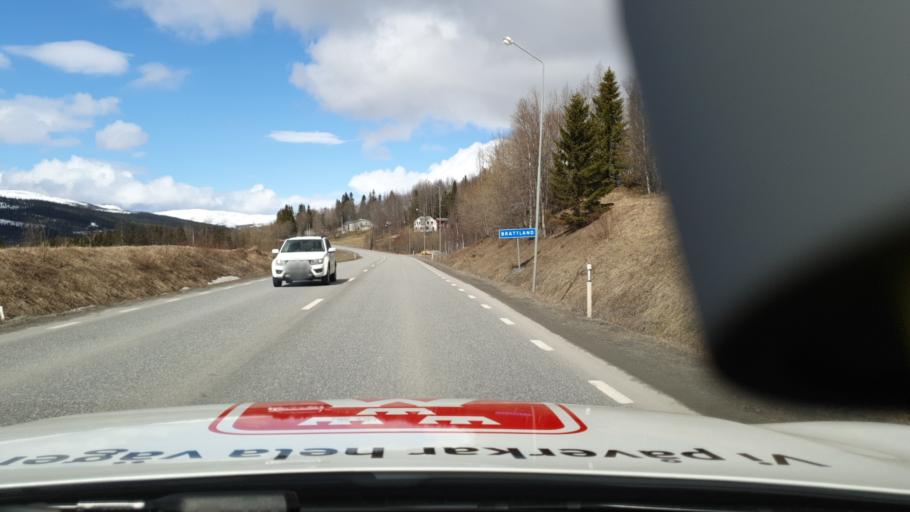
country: SE
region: Jaemtland
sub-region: Are Kommun
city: Are
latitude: 63.3394
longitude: 13.2073
